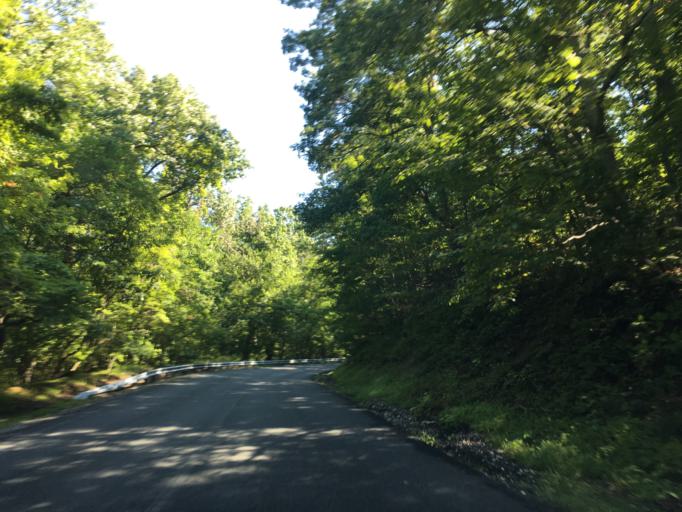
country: US
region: Pennsylvania
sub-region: York County
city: New Freedom
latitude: 39.6225
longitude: -76.7077
